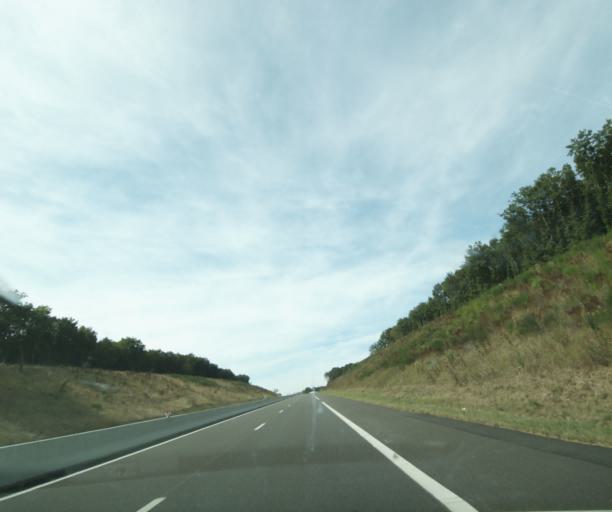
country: FR
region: Auvergne
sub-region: Departement de l'Allier
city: Vendat
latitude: 46.1416
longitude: 3.3300
